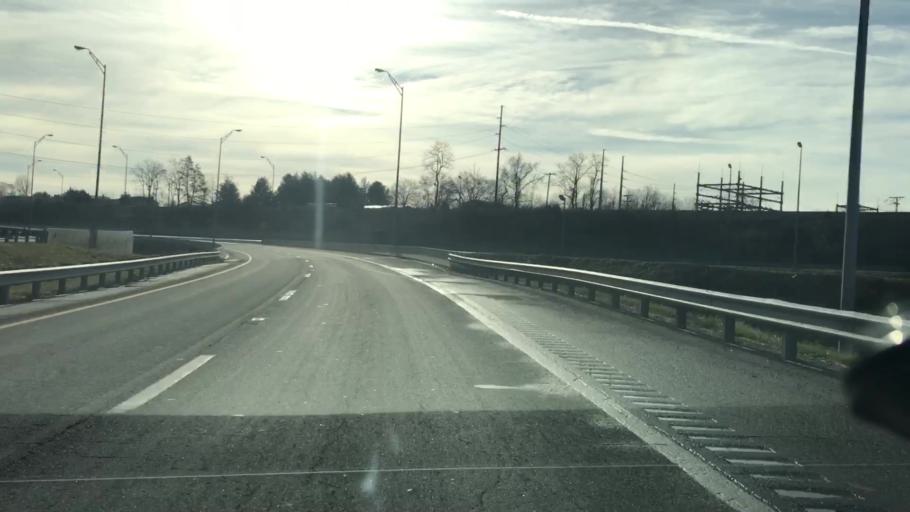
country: US
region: Virginia
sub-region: Montgomery County
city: Christiansburg
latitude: 37.1540
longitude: -80.4116
